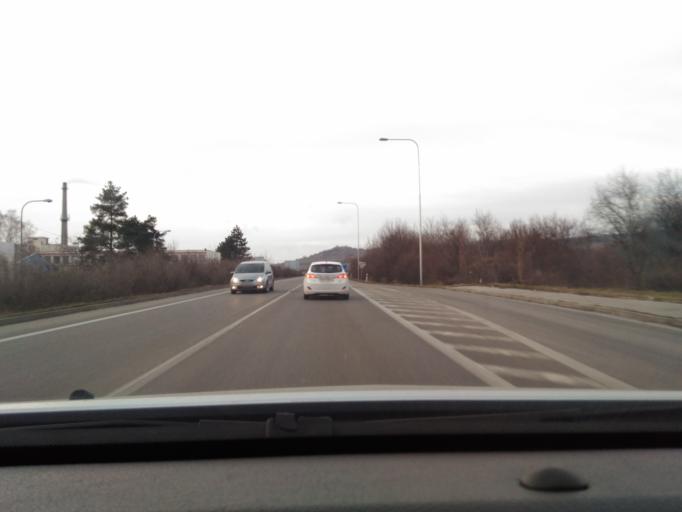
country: CZ
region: South Moravian
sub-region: Okres Breclav
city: Mikulov
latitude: 48.8087
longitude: 16.6260
